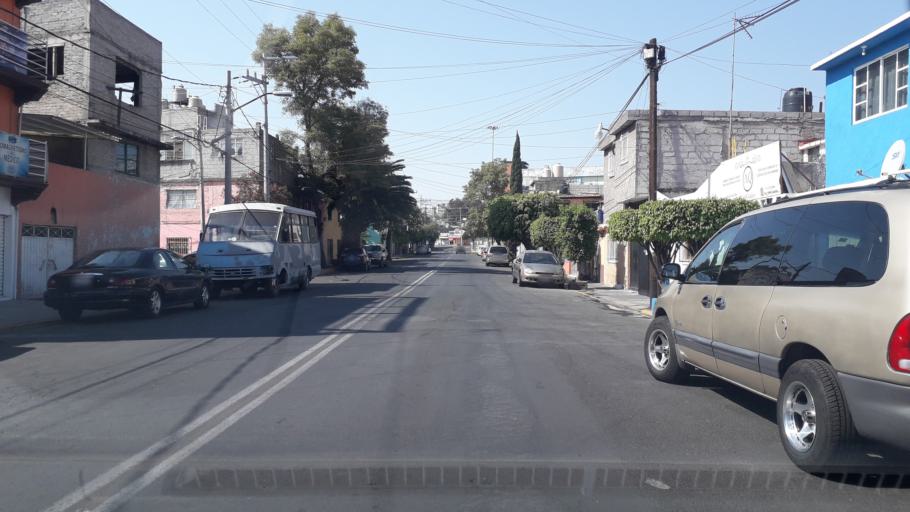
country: MX
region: Mexico City
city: Gustavo A. Madero
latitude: 19.5058
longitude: -99.0960
